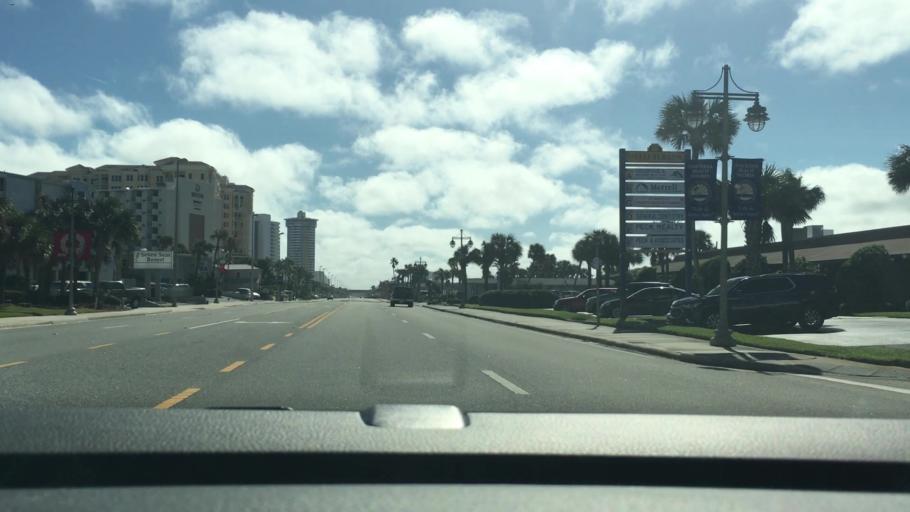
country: US
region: Florida
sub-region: Volusia County
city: Daytona Beach Shores
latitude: 29.1891
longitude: -80.9895
